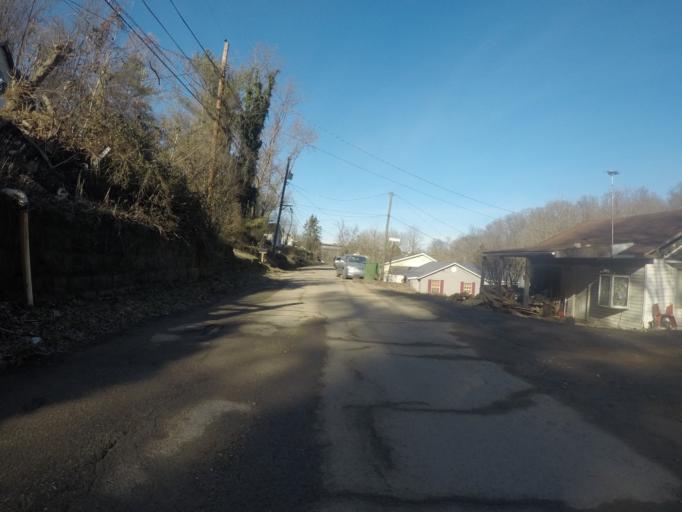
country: US
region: West Virginia
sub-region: Cabell County
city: Huntington
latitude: 38.3977
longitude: -82.4874
